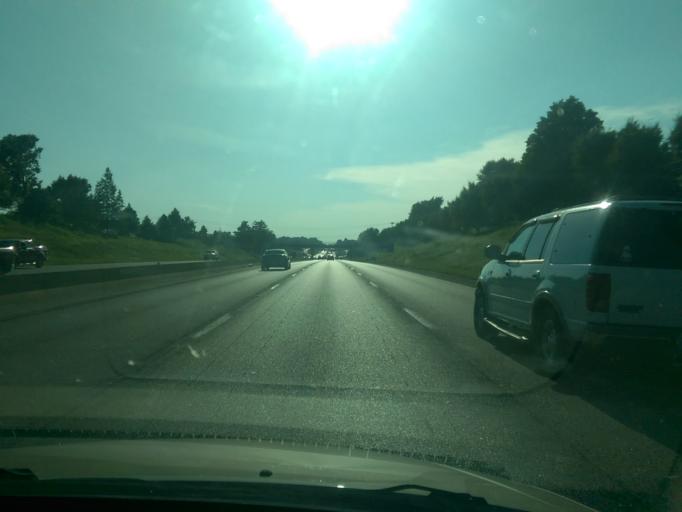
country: US
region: Missouri
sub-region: Jackson County
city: Independence
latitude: 39.0455
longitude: -94.4021
